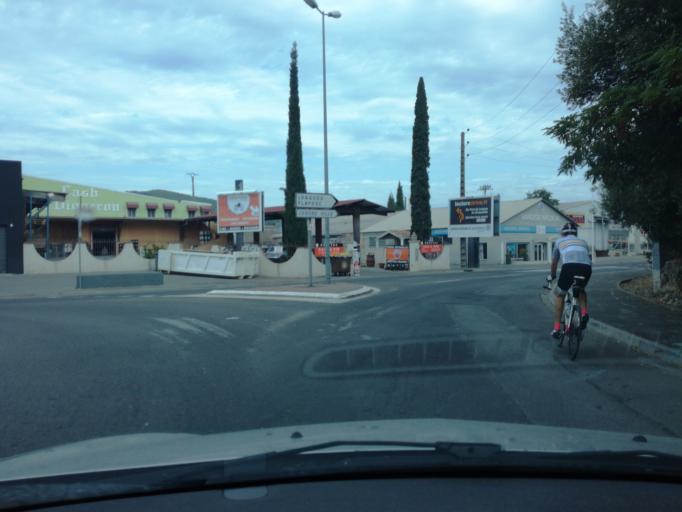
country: FR
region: Provence-Alpes-Cote d'Azur
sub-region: Departement du Var
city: Draguignan
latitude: 43.5281
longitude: 6.4492
